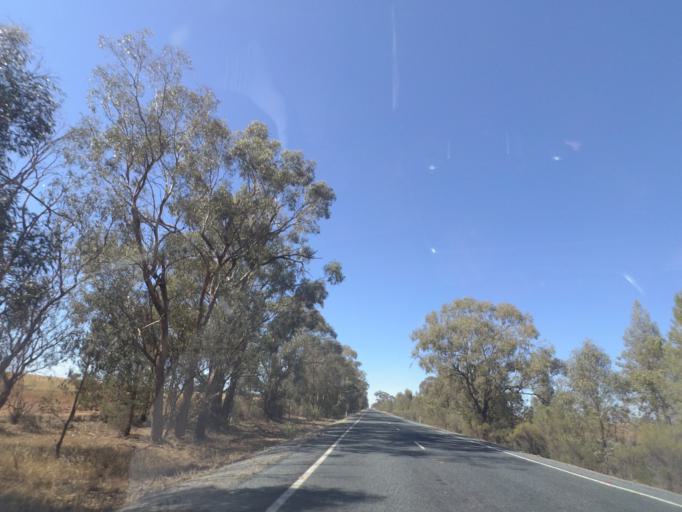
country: AU
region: New South Wales
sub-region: Bland
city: West Wyalong
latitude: -34.1505
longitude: 147.1185
